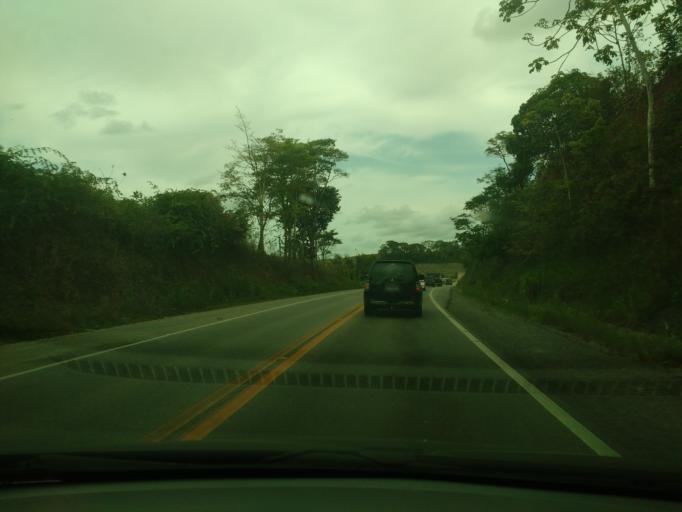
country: BR
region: Alagoas
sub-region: Messias
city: Messias
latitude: -9.3682
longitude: -35.8380
